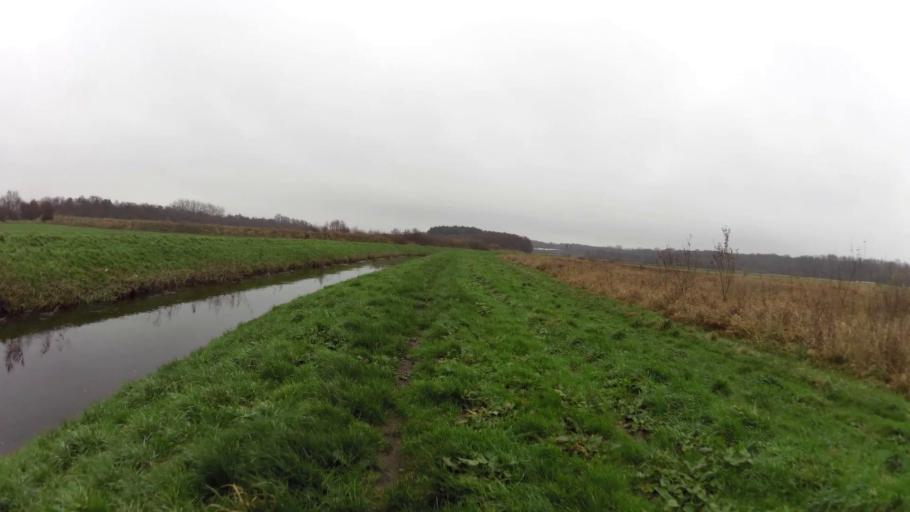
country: PL
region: West Pomeranian Voivodeship
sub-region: Koszalin
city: Koszalin
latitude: 54.2398
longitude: 16.1378
